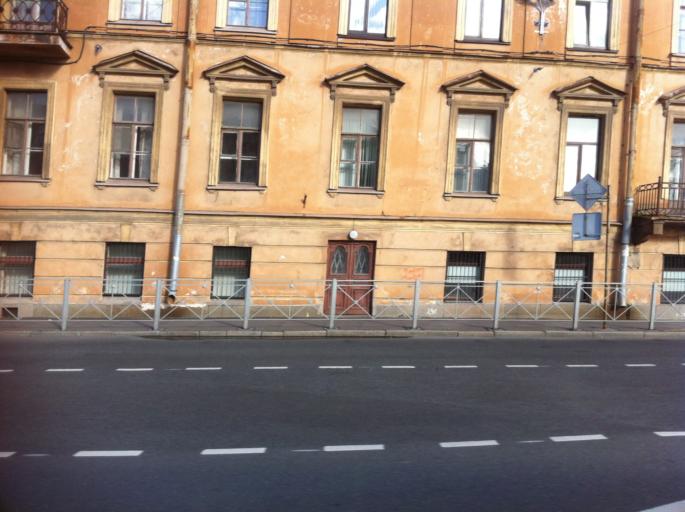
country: RU
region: St.-Petersburg
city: Admiralteisky
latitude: 59.9179
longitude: 30.2801
